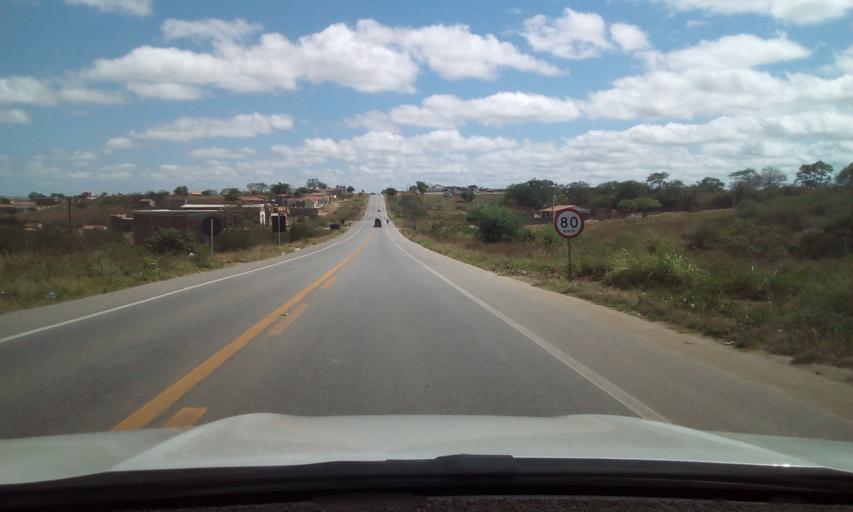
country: BR
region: Paraiba
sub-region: Campina Grande
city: Campina Grande
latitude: -7.3450
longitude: -35.9000
